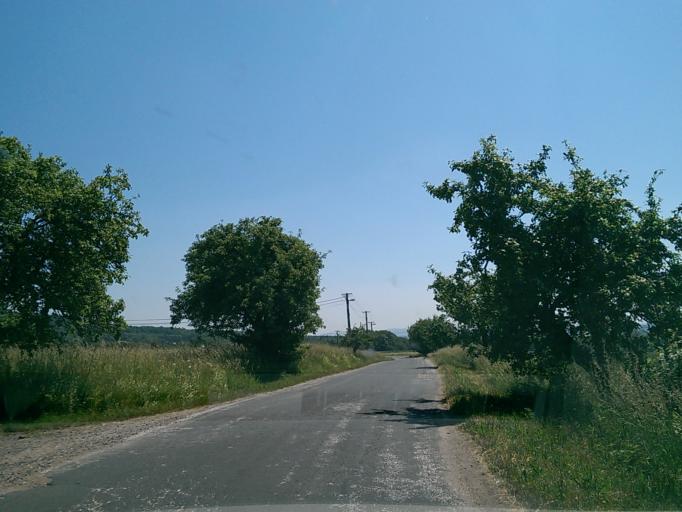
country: CZ
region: Liberecky
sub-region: Okres Semily
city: Lomnice nad Popelkou
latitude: 50.5003
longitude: 15.3349
